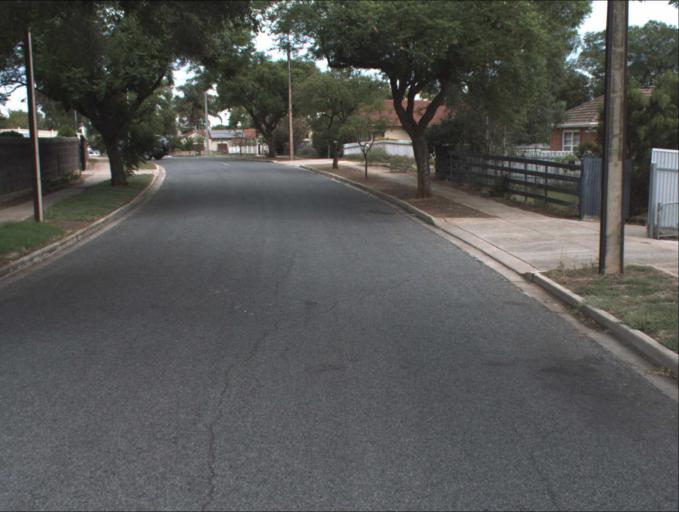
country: AU
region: South Australia
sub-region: Port Adelaide Enfield
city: Enfield
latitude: -34.8589
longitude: 138.6034
